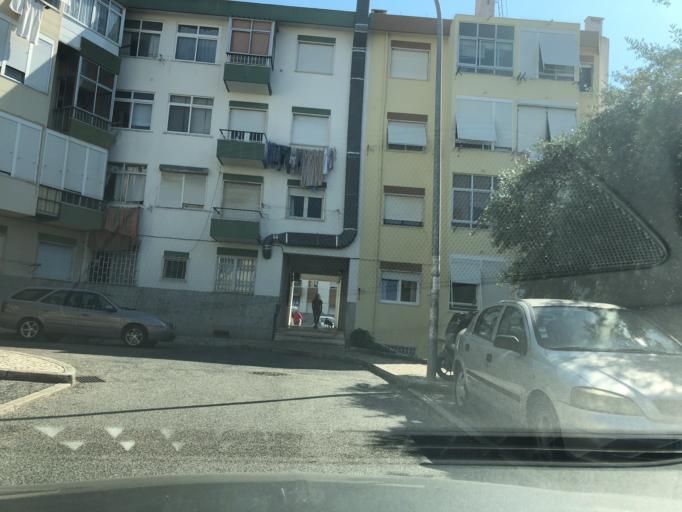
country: PT
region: Lisbon
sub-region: Oeiras
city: Carnaxide
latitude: 38.7262
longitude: -9.2448
